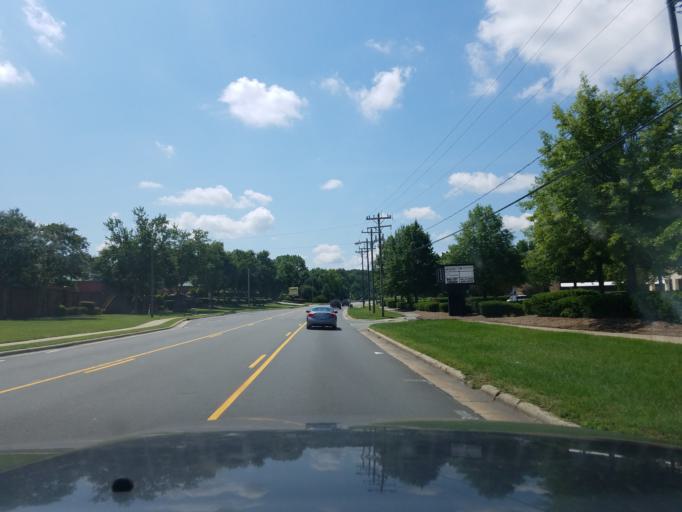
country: US
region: North Carolina
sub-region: Durham County
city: Durham
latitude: 35.9592
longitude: -78.9751
